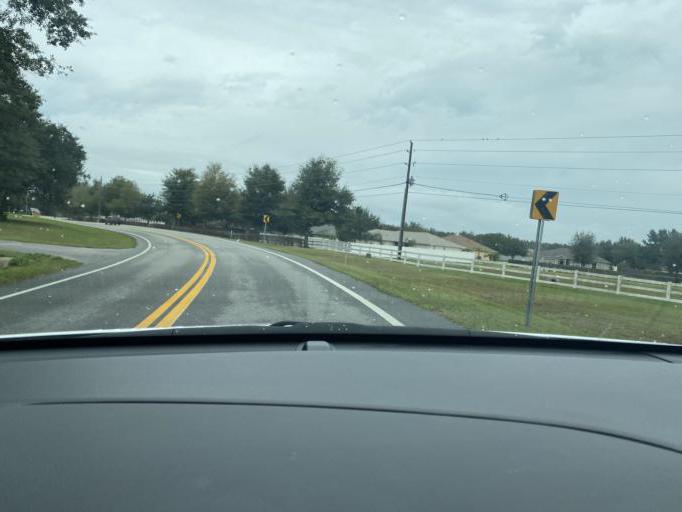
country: US
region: Florida
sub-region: Lake County
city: Mascotte
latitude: 28.5803
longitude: -81.8688
